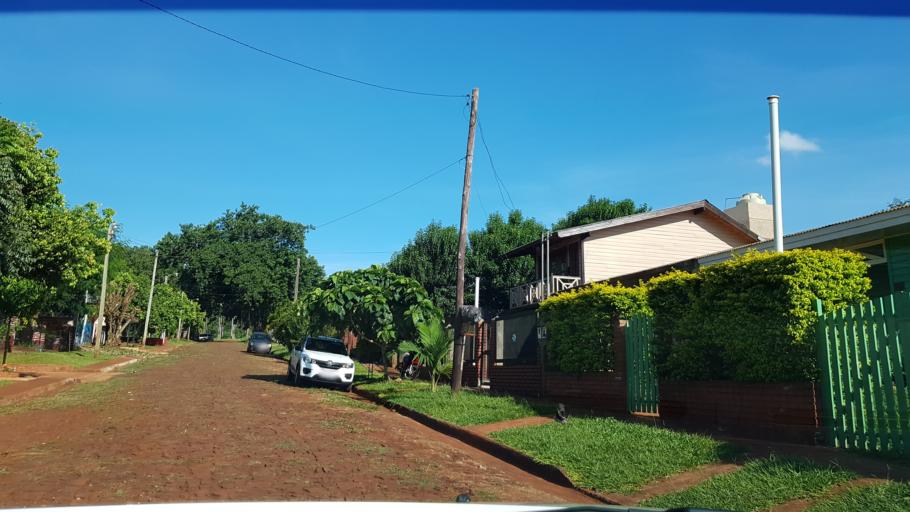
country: AR
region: Misiones
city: Puerto Libertad
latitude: -25.9154
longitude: -54.5797
